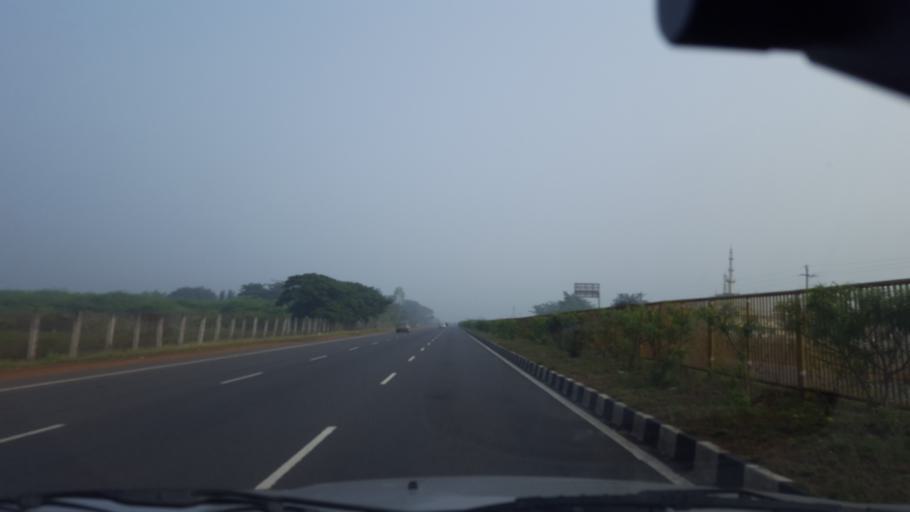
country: IN
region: Andhra Pradesh
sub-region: Prakasam
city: Ongole
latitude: 15.4342
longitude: 80.0439
